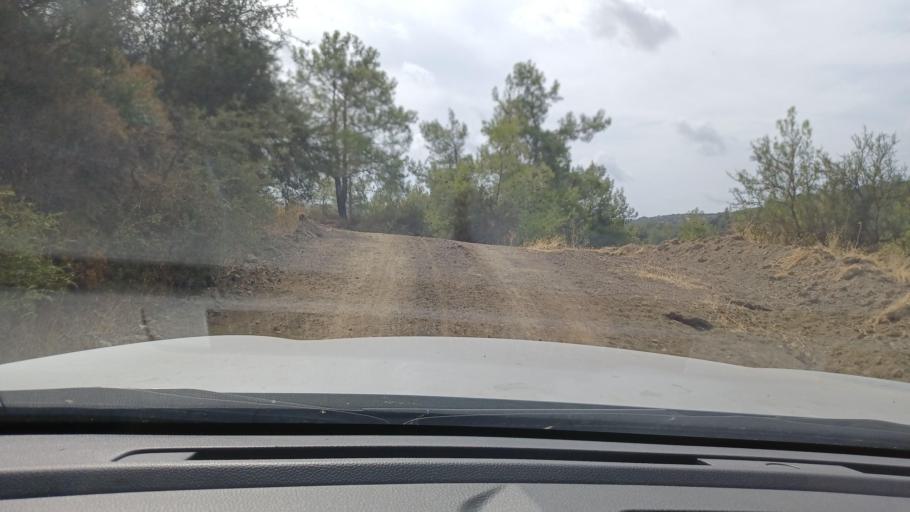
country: CY
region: Pafos
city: Polis
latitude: 35.0072
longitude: 32.5408
